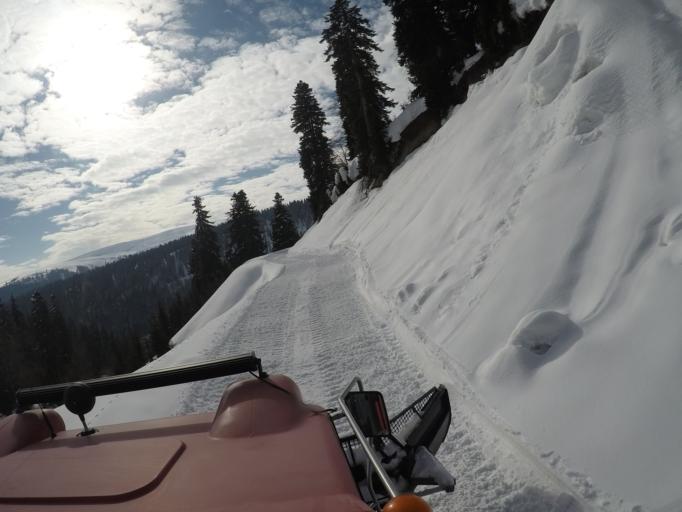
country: GE
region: Ajaria
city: Dioknisi
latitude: 41.6357
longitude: 42.5470
